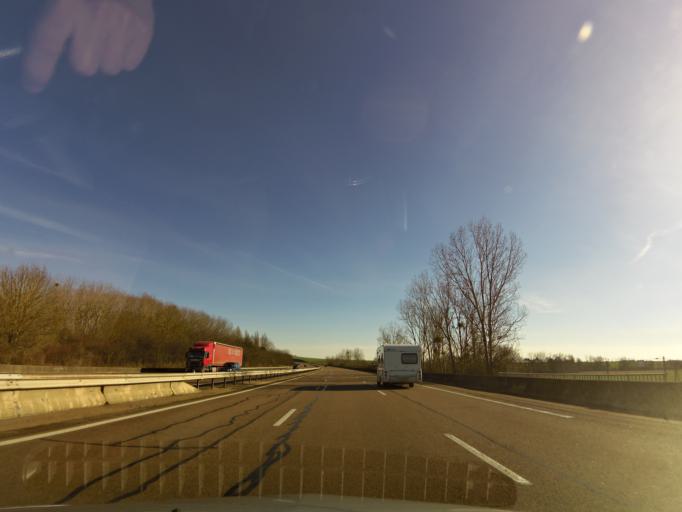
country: FR
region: Bourgogne
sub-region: Departement de l'Yonne
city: Aillant-sur-Tholon
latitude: 47.9019
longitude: 3.3504
